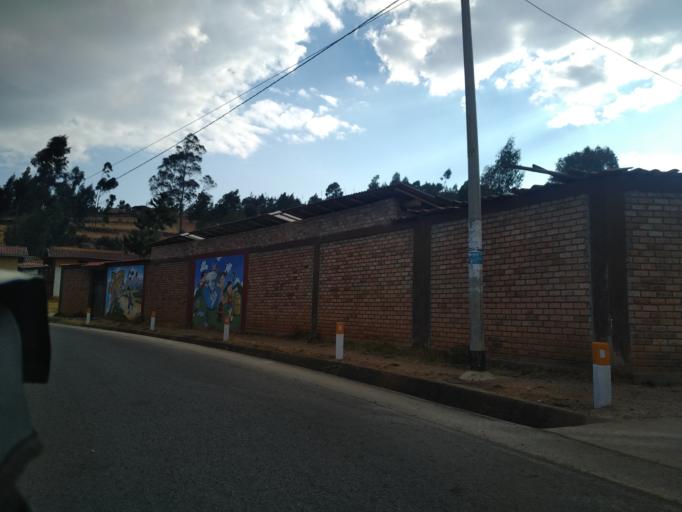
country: PE
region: Cajamarca
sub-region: Provincia de Cajamarca
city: Llacanora
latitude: -7.1438
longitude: -78.4105
